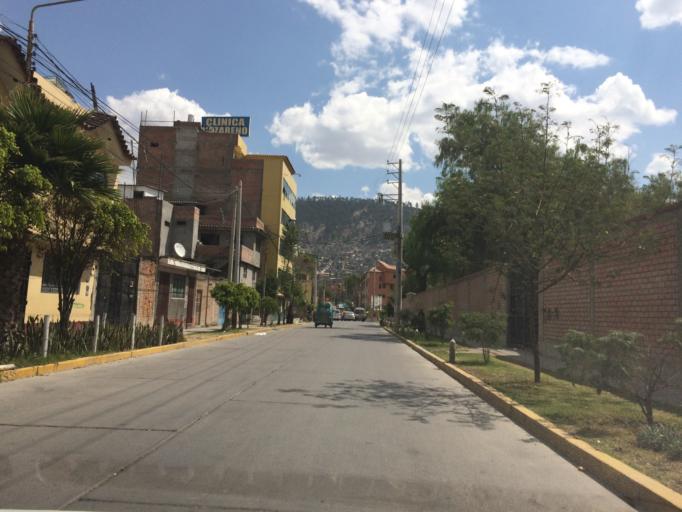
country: PE
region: Ayacucho
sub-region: Provincia de Huamanga
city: Ayacucho
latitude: -13.1554
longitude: -74.2226
